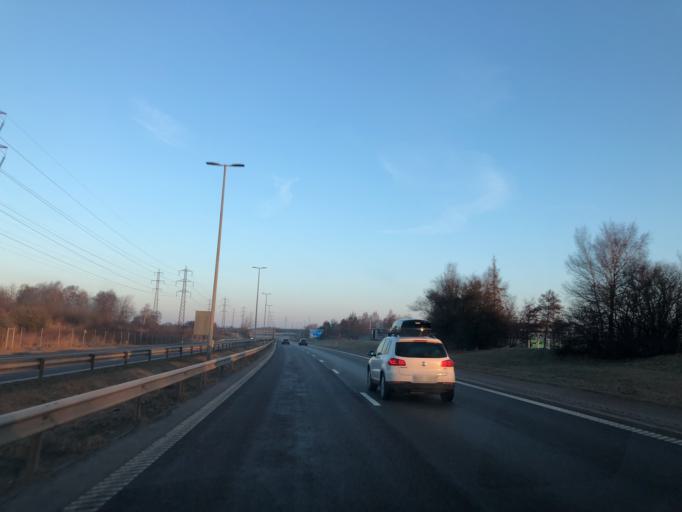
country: SE
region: Halland
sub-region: Halmstads Kommun
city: Fyllinge
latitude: 56.6672
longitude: 12.9046
